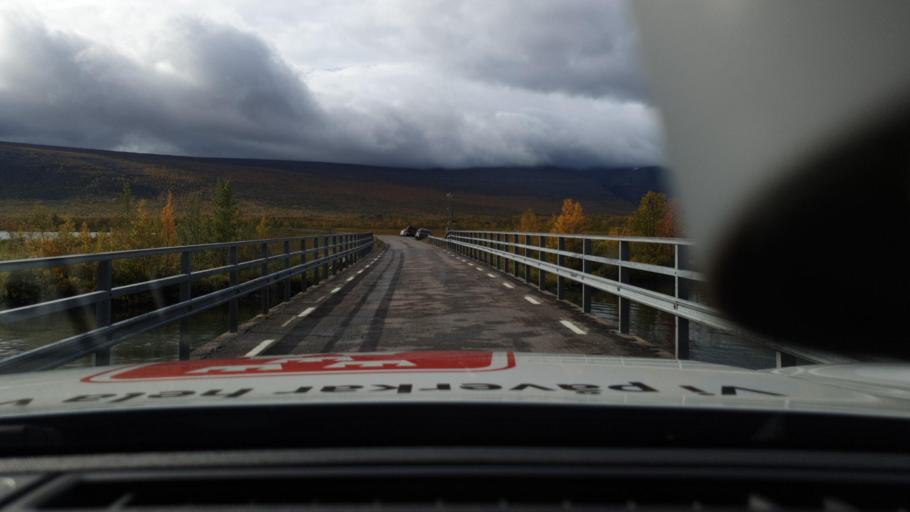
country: SE
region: Norrbotten
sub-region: Kiruna Kommun
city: Kiruna
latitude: 67.8610
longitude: 19.0294
